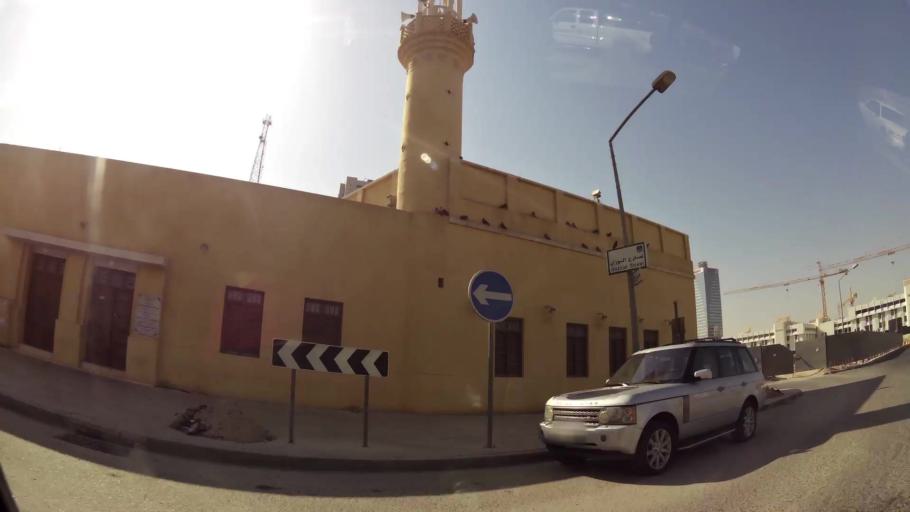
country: KW
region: Al Asimah
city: Kuwait City
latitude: 29.3671
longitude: 47.9794
